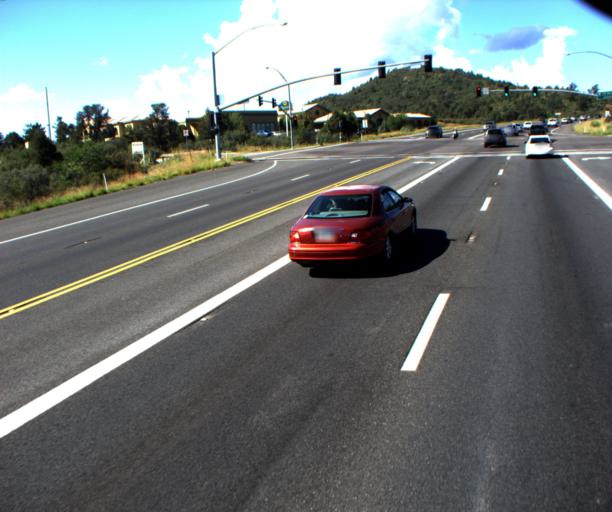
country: US
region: Arizona
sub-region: Yavapai County
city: Prescott
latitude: 34.5528
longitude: -112.3837
